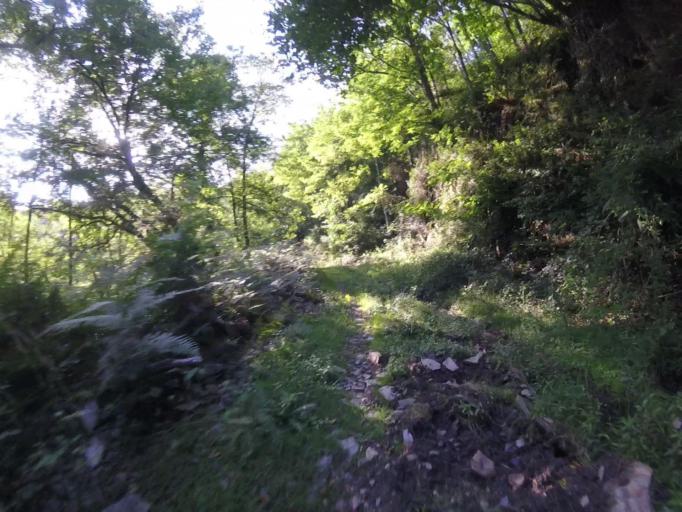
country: ES
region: Navarre
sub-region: Provincia de Navarra
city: Arano
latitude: 43.2271
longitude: -1.9095
